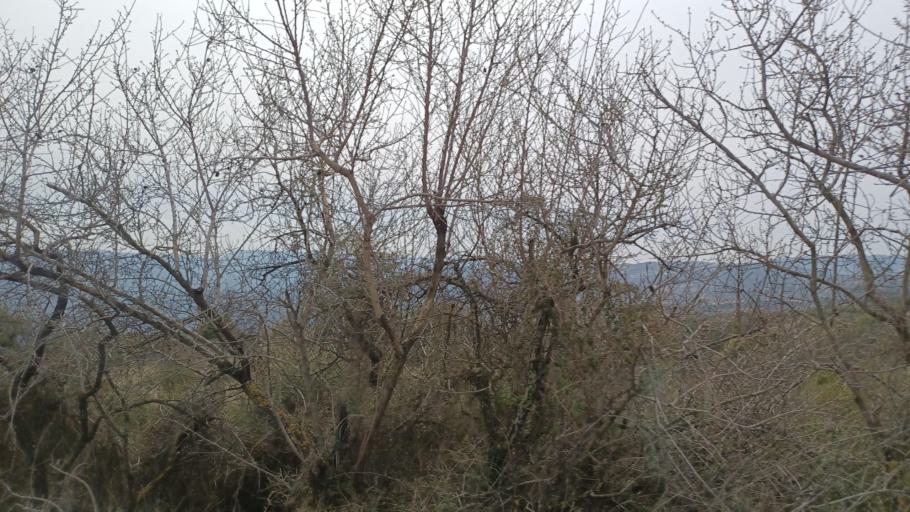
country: CY
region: Limassol
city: Pachna
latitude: 34.8590
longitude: 32.7046
